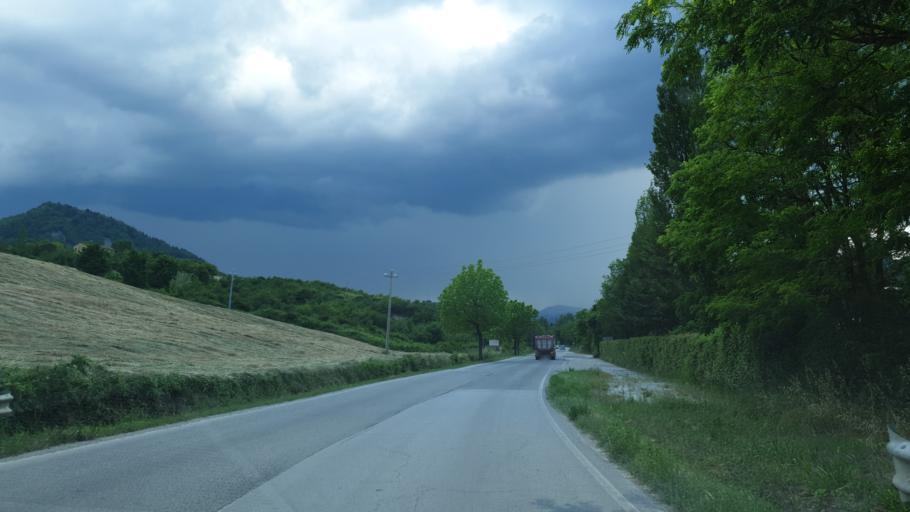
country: IT
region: Emilia-Romagna
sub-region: Provincia di Rimini
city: Pietracuta
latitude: 43.9454
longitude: 12.3601
